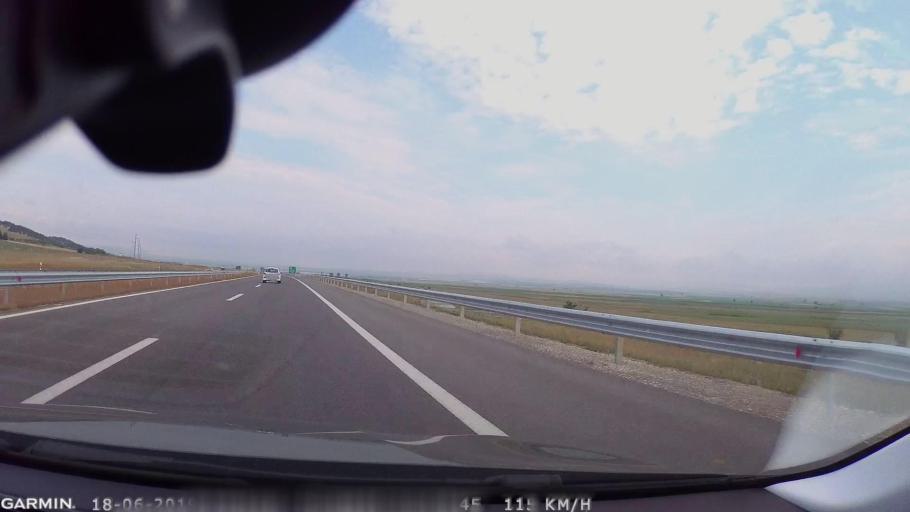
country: MK
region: Sveti Nikole
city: Sveti Nikole
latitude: 41.8047
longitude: 22.0699
